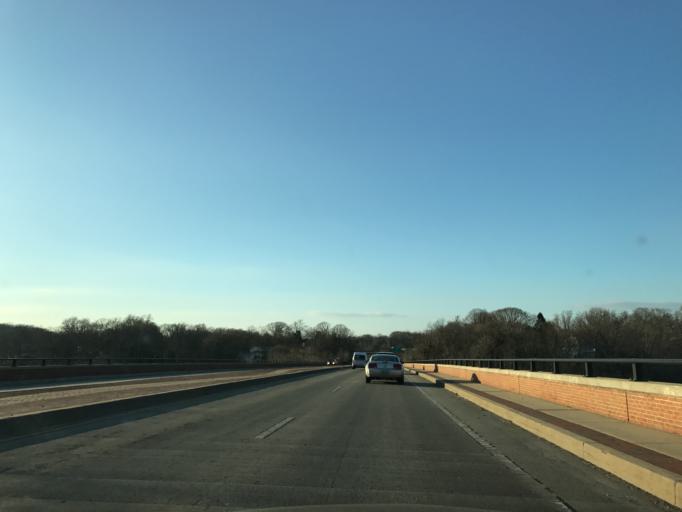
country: US
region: Maryland
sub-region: Anne Arundel County
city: Annapolis
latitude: 38.9904
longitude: -76.5081
